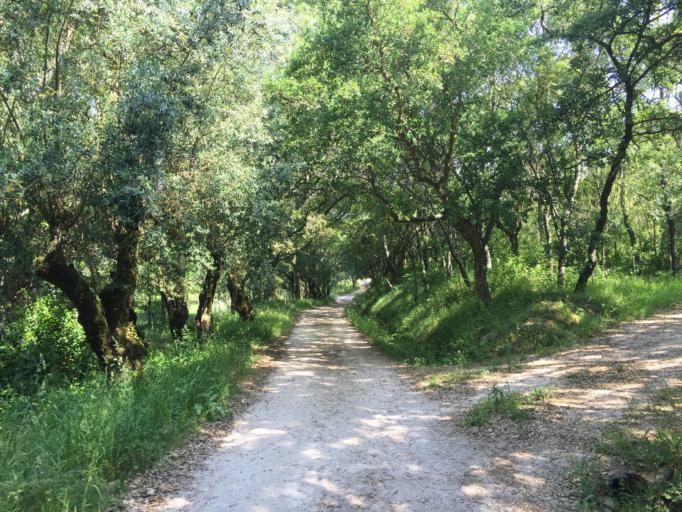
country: PT
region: Lisbon
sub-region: Mafra
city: Milharado
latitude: 38.9035
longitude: -9.1864
